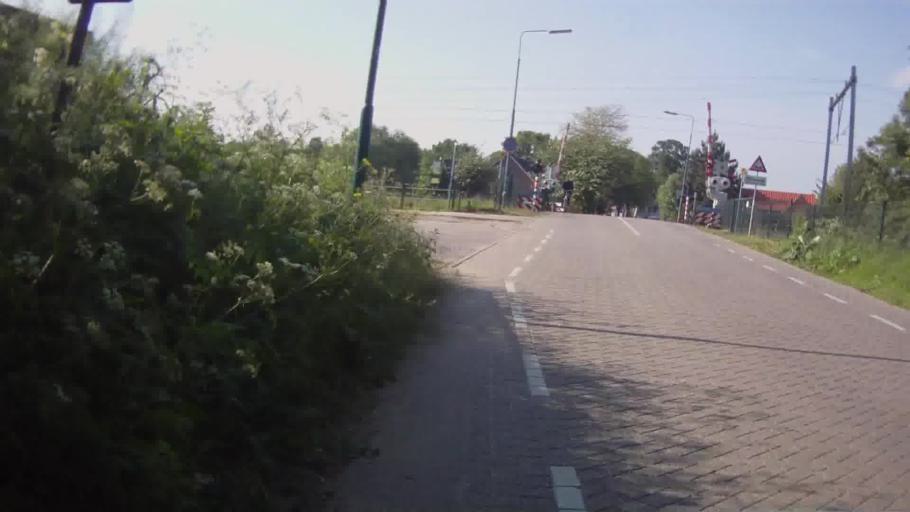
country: NL
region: Utrecht
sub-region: Gemeente Bunnik
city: Bunnik
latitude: 52.0621
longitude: 5.1726
